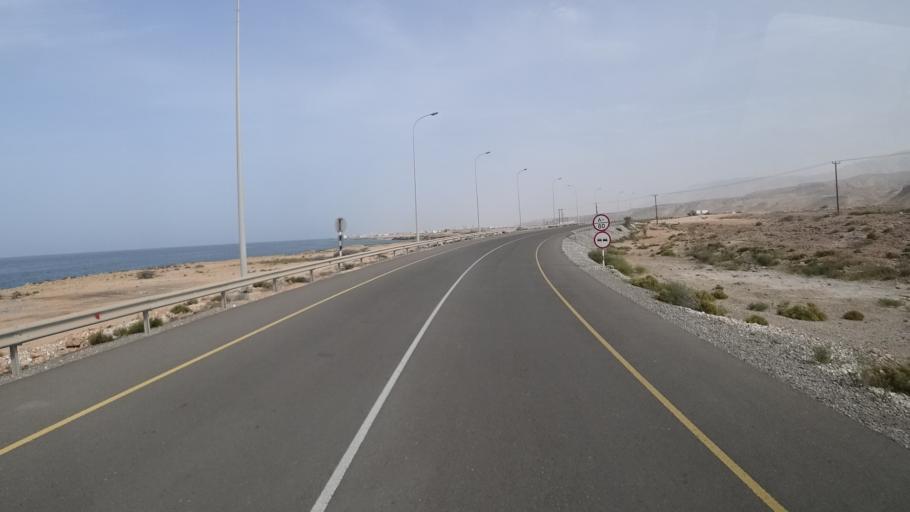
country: OM
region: Ash Sharqiyah
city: Sur
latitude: 23.0045
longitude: 59.1169
